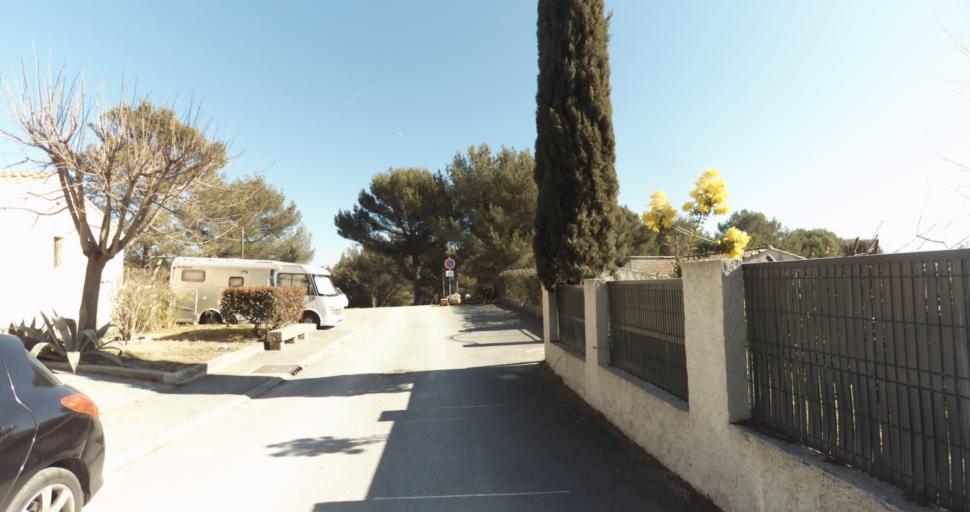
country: FR
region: Provence-Alpes-Cote d'Azur
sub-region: Departement des Bouches-du-Rhone
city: Peypin
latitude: 43.3894
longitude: 5.5671
